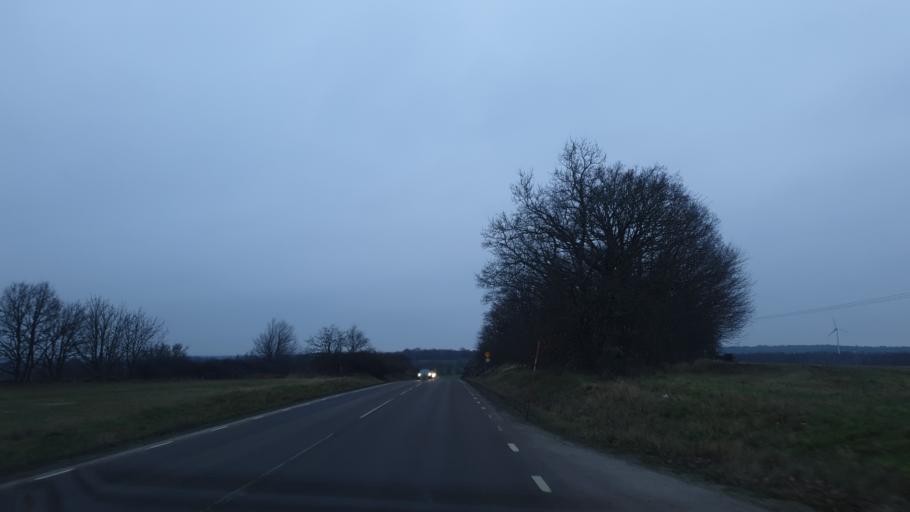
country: SE
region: Blekinge
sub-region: Karlskrona Kommun
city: Jaemjoe
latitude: 56.1519
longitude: 15.7615
